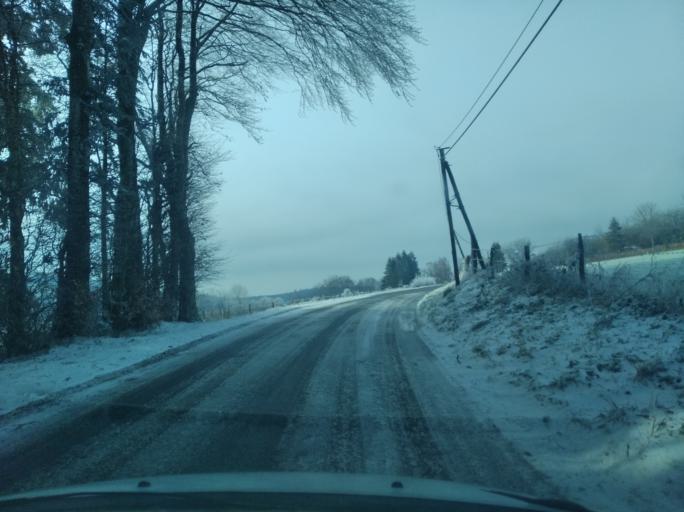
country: FR
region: Rhone-Alpes
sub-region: Departement de la Loire
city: Ambierle
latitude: 46.1089
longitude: 3.8102
